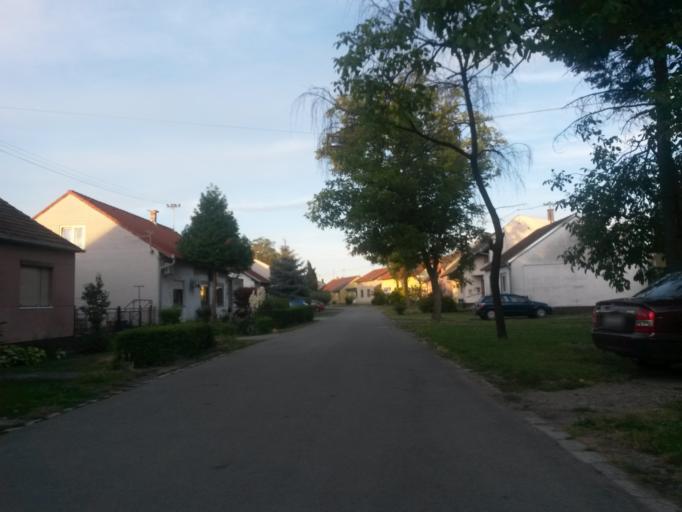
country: HR
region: Osjecko-Baranjska
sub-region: Grad Osijek
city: Osijek
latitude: 45.5457
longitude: 18.7045
